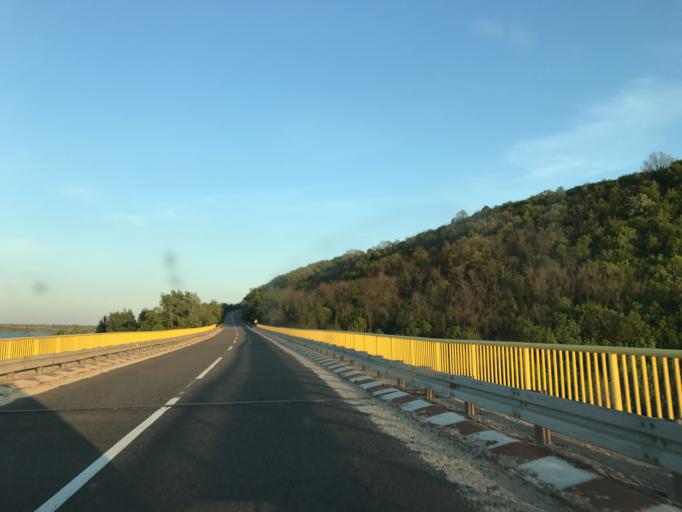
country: RO
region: Mehedinti
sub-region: Comuna Gogosu
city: Ostrovu Mare
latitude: 44.4283
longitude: 22.4690
